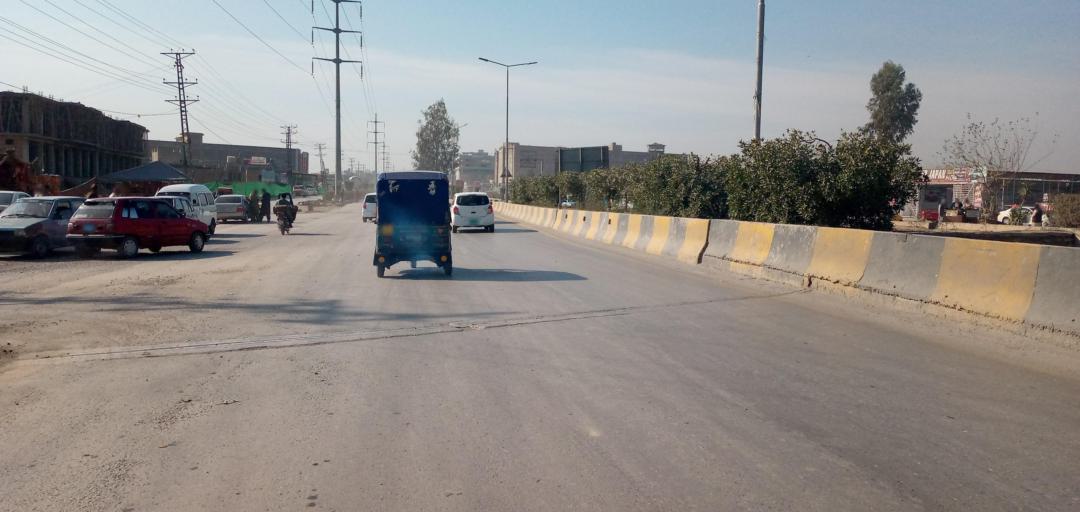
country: PK
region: Khyber Pakhtunkhwa
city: Peshawar
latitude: 33.9688
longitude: 71.5379
